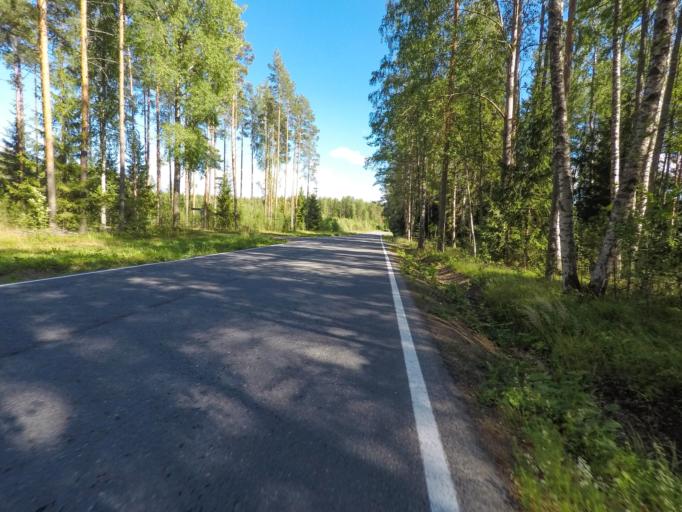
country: FI
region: South Karelia
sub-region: Lappeenranta
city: Taipalsaari
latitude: 61.1795
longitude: 28.0060
